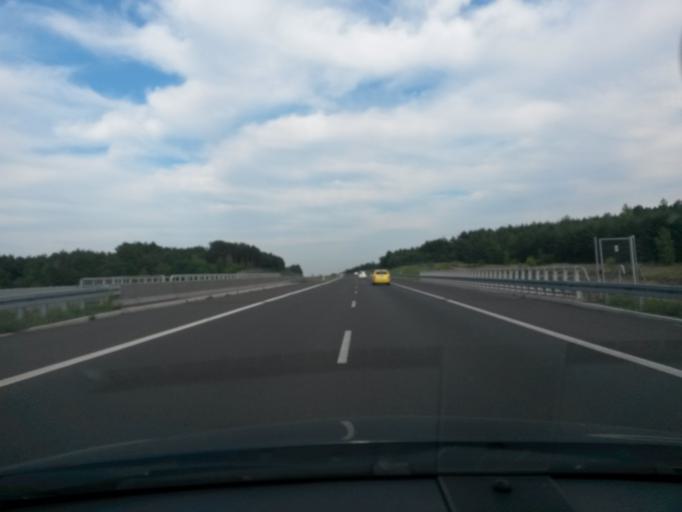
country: PL
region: Greater Poland Voivodeship
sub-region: Powiat kolski
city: Koscielec
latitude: 52.1415
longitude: 18.5404
